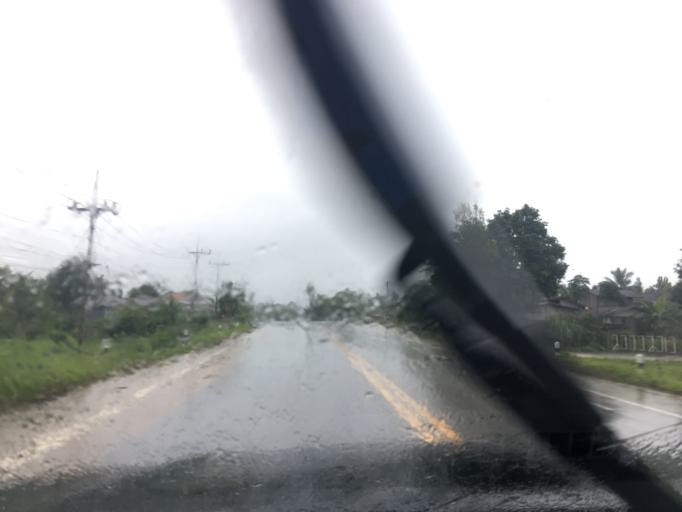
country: TH
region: Chiang Rai
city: Chiang Saen
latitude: 20.2855
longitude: 100.2179
